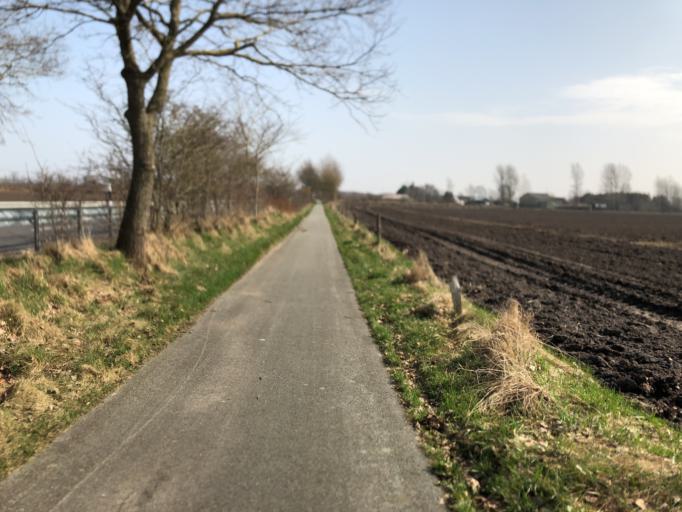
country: DE
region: Schleswig-Holstein
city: Jerrishoe
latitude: 54.6768
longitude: 9.3689
